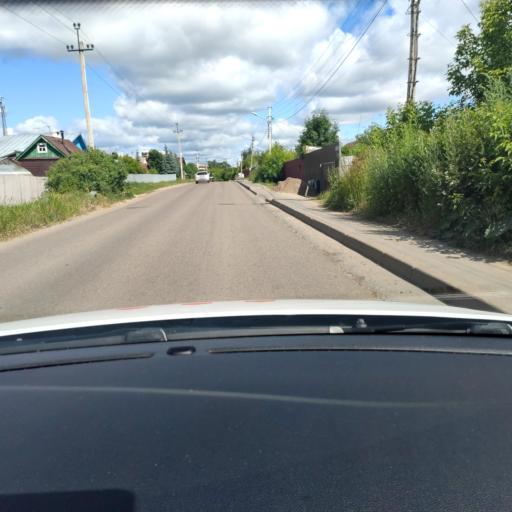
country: RU
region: Tatarstan
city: Vysokaya Gora
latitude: 55.8628
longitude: 49.2381
